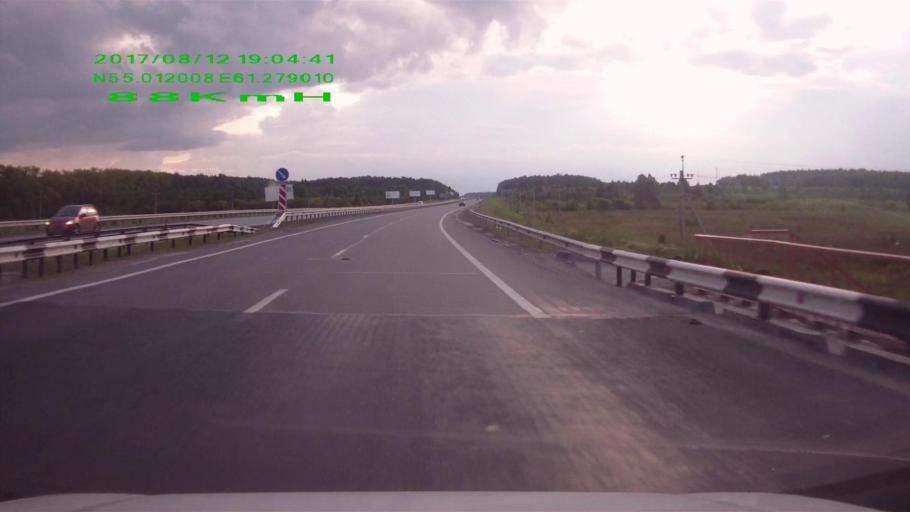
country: RU
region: Chelyabinsk
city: Sargazy
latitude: 55.0114
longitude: 61.2611
